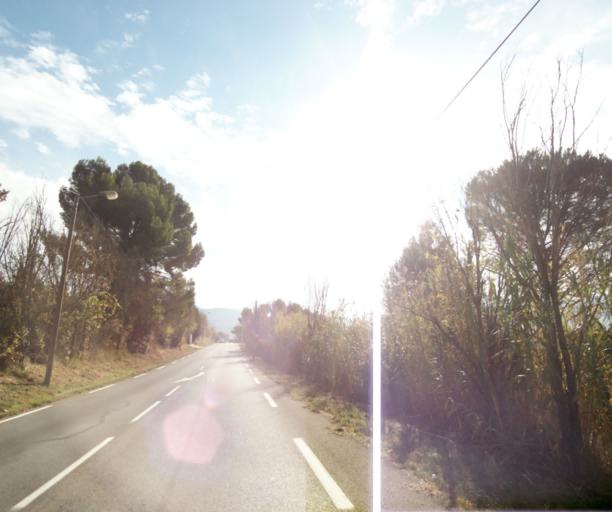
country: FR
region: Provence-Alpes-Cote d'Azur
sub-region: Departement des Bouches-du-Rhone
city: Gemenos
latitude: 43.3075
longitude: 5.6097
